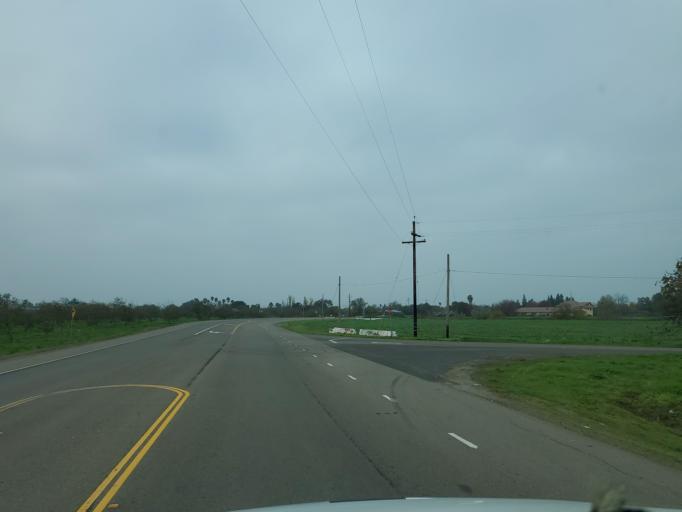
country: US
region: California
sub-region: San Joaquin County
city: Garden Acres
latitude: 37.9466
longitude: -121.2399
